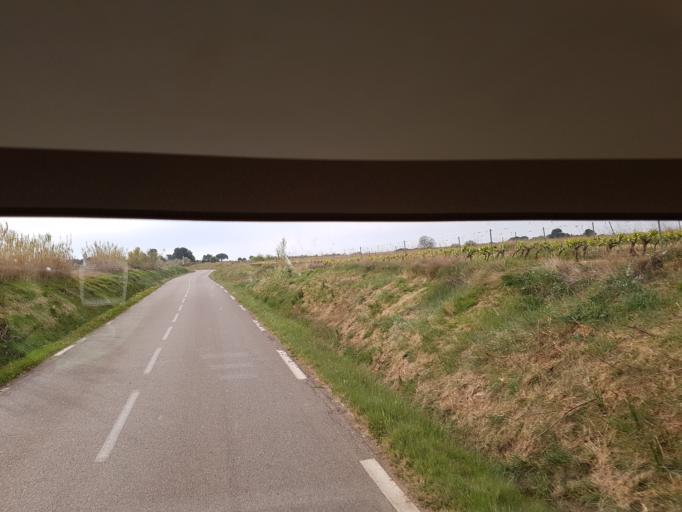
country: FR
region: Languedoc-Roussillon
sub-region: Departement de l'Herault
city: Marseillan
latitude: 43.3669
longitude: 3.5110
